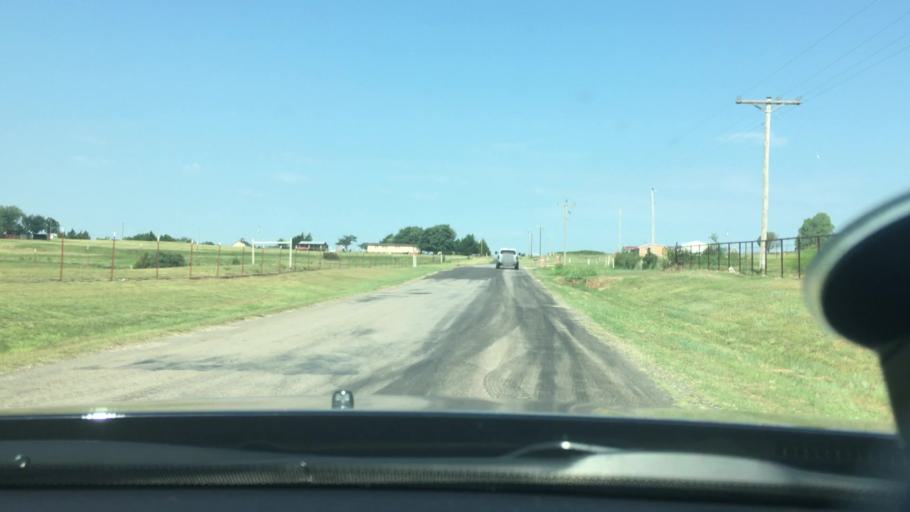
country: US
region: Oklahoma
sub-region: Garvin County
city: Lindsay
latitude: 34.7829
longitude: -97.6055
